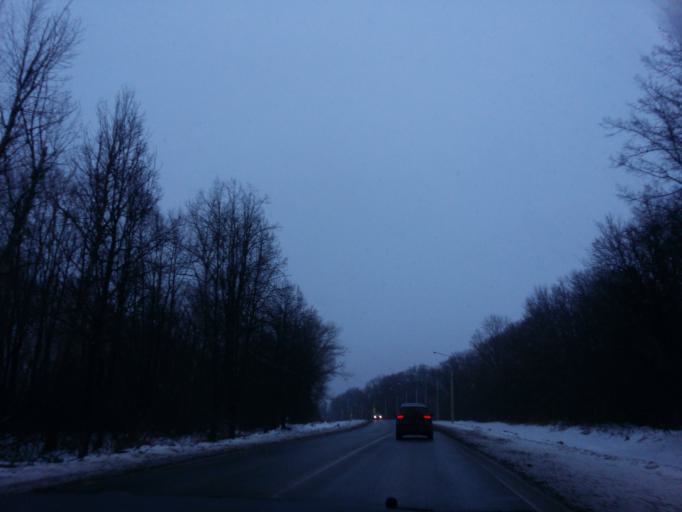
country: RU
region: Tula
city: Pervomayskiy
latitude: 54.0683
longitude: 37.5370
